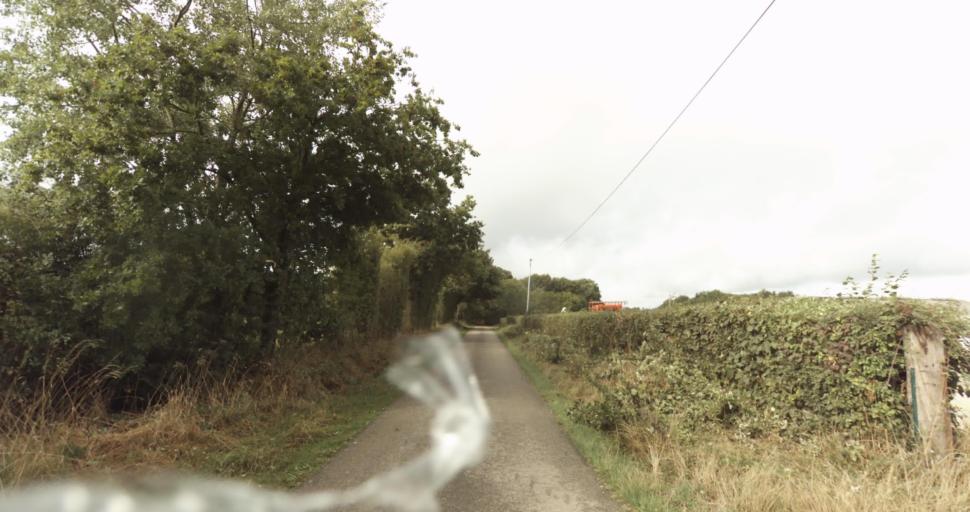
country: FR
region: Lower Normandy
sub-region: Departement de l'Orne
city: Gace
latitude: 48.8557
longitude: 0.3176
